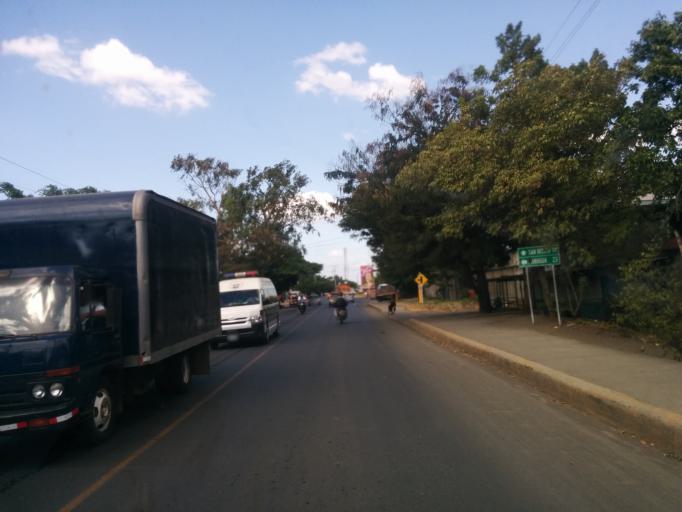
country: NI
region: Managua
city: Tipitapa
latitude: 12.1892
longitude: -86.0967
